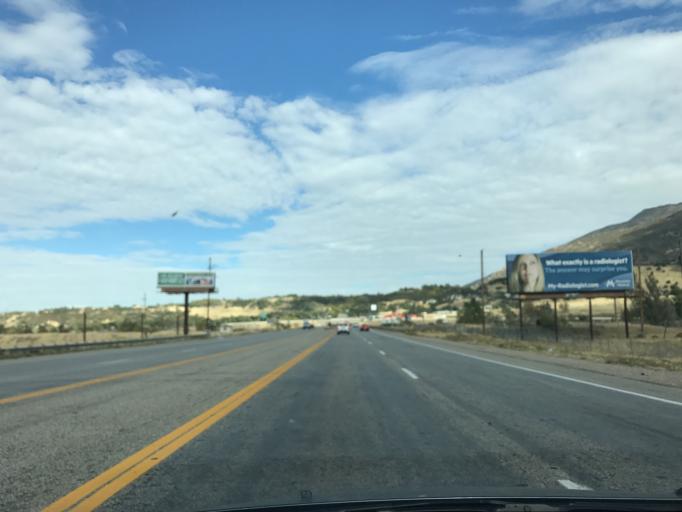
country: US
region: Utah
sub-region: Weber County
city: Uintah
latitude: 41.1327
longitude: -111.9108
